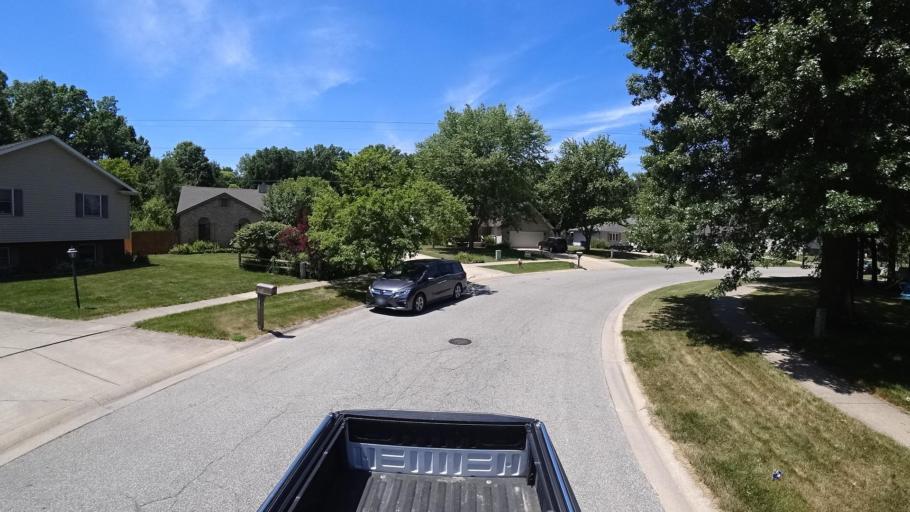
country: US
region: Indiana
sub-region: Porter County
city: Porter
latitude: 41.6016
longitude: -87.0984
